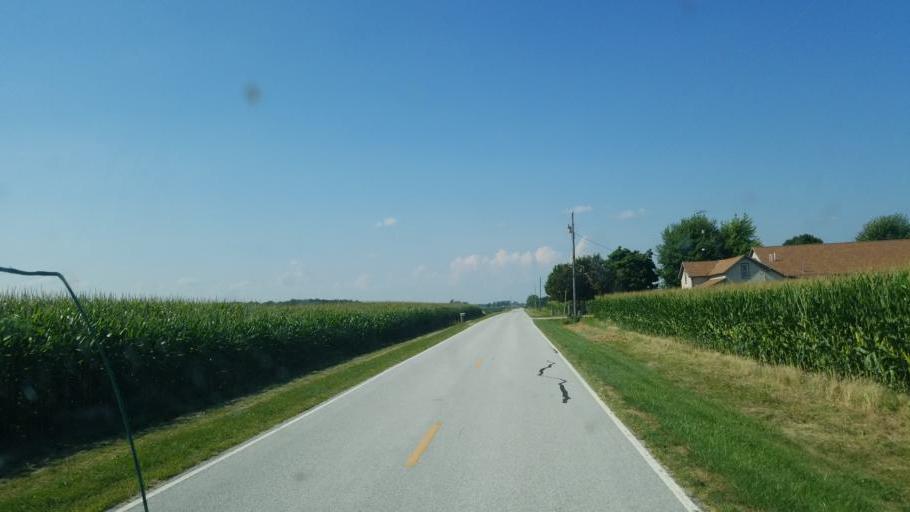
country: US
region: Ohio
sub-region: Hardin County
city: Forest
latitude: 40.7181
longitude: -83.4958
